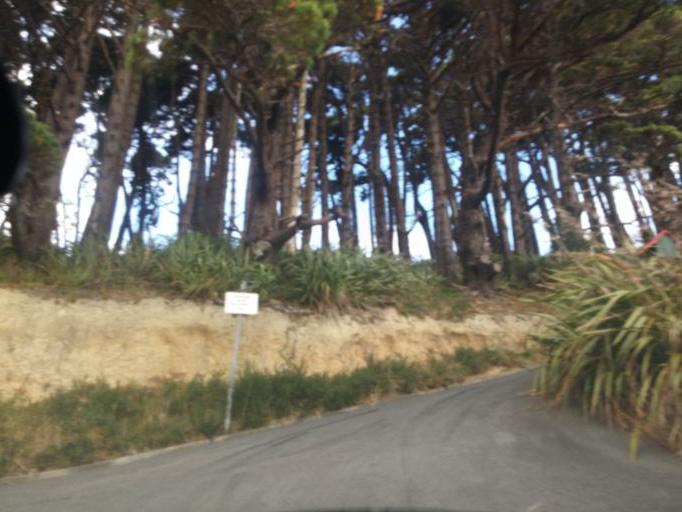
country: NZ
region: Wellington
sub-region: Wellington City
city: Kelburn
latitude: -41.2657
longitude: 174.7719
